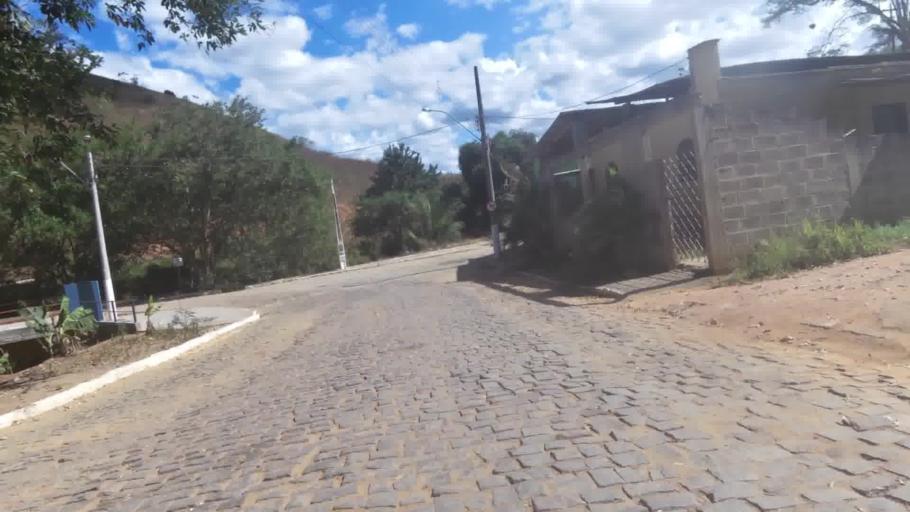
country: BR
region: Espirito Santo
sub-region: Cachoeiro De Itapemirim
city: Cachoeiro de Itapemirim
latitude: -20.9160
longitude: -41.1991
